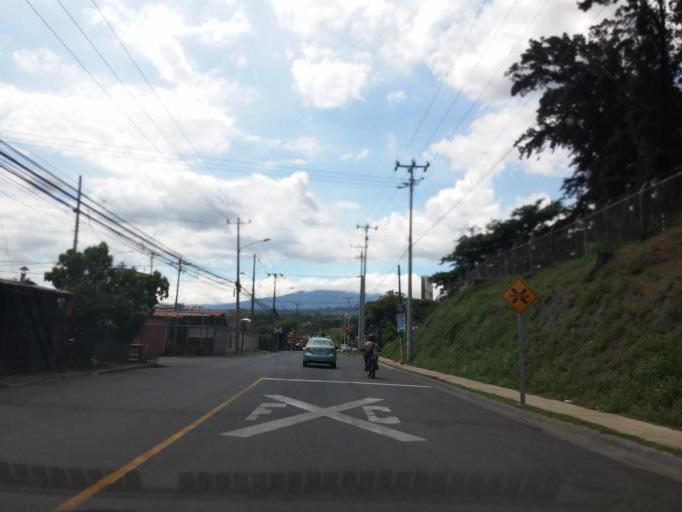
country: CR
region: Heredia
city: Llorente
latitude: 10.0020
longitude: -84.1706
